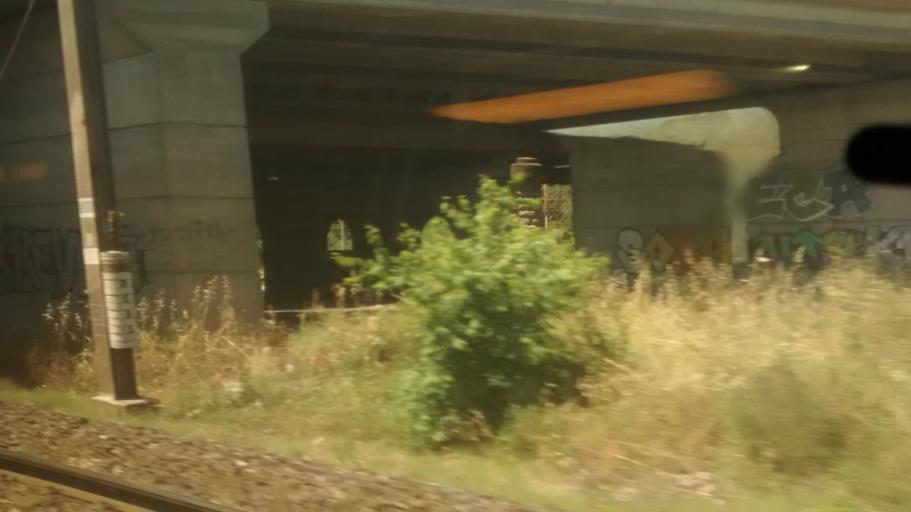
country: FR
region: Languedoc-Roussillon
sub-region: Departement du Gard
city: Rodilhan
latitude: 43.8480
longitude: 4.3990
